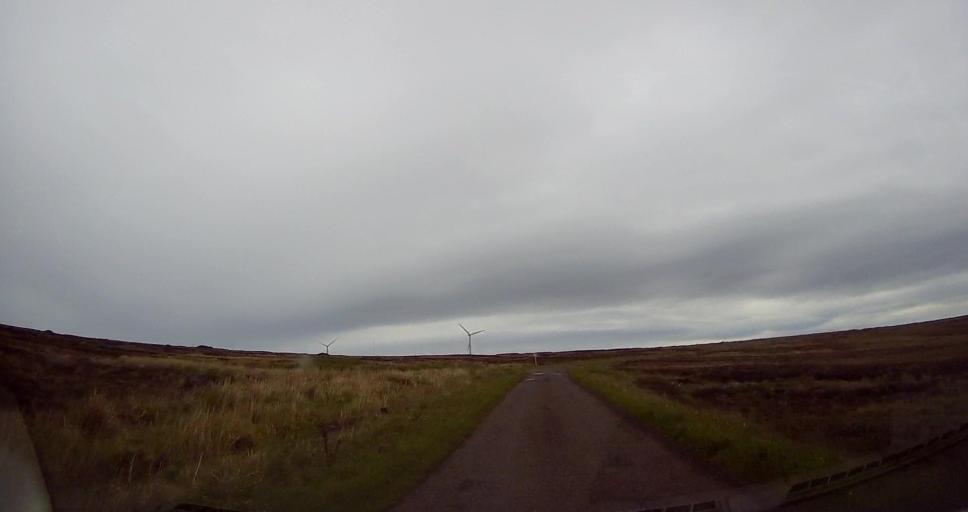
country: GB
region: Scotland
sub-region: Orkney Islands
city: Stromness
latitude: 59.0996
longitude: -3.1491
